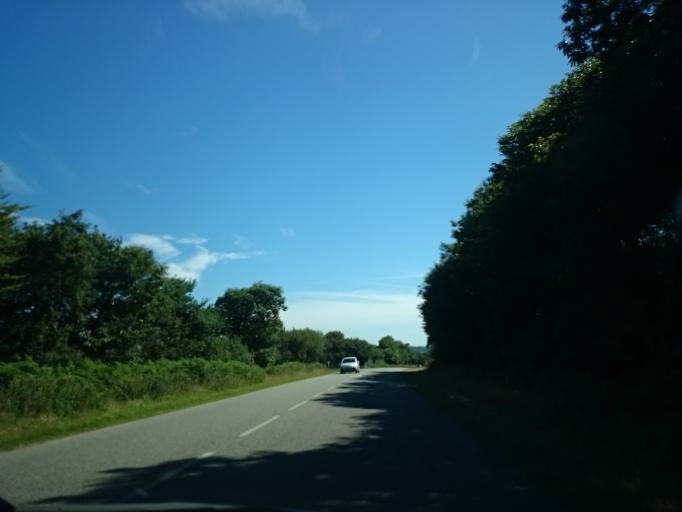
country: FR
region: Brittany
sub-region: Departement du Finistere
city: Lanrivoare
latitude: 48.4357
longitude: -4.6727
